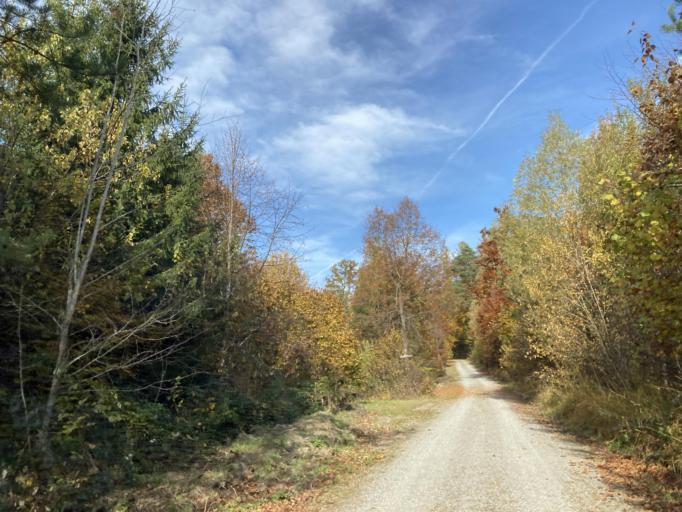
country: DE
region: Baden-Wuerttemberg
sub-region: Tuebingen Region
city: Bodelshausen
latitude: 48.4301
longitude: 8.9704
